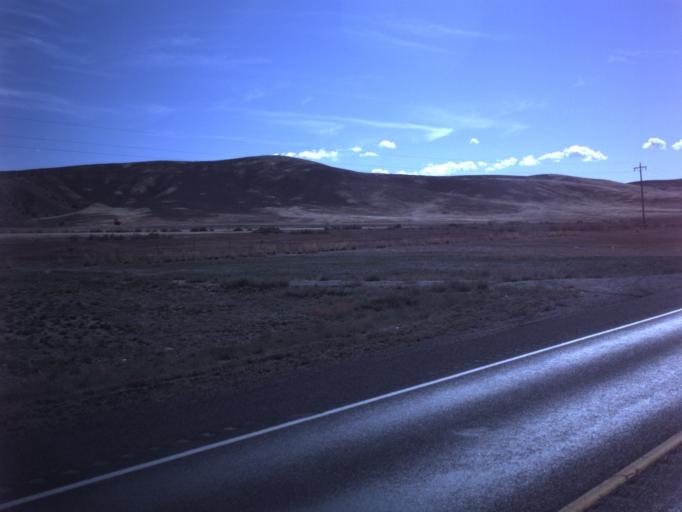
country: US
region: Utah
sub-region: Sanpete County
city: Gunnison
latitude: 39.1940
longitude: -111.8440
